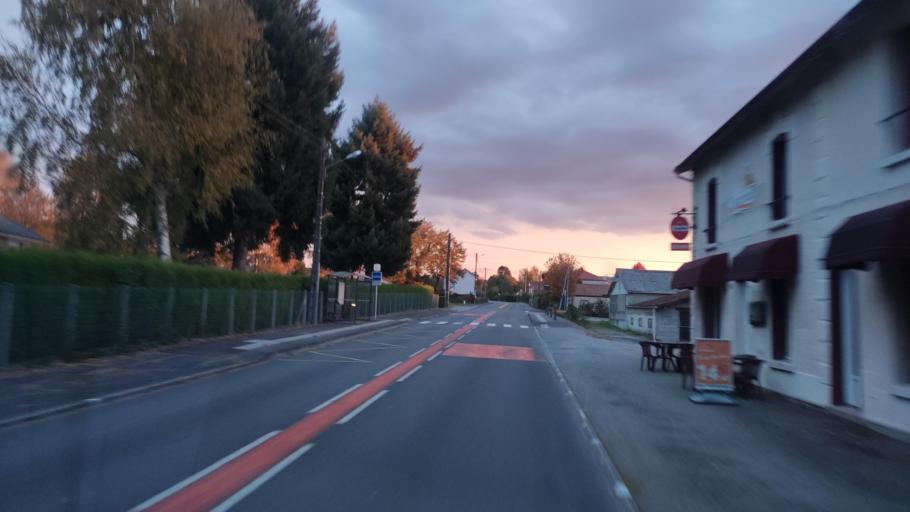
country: FR
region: Limousin
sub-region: Departement de la Haute-Vienne
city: Rilhac-Rancon
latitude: 45.9240
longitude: 1.3424
